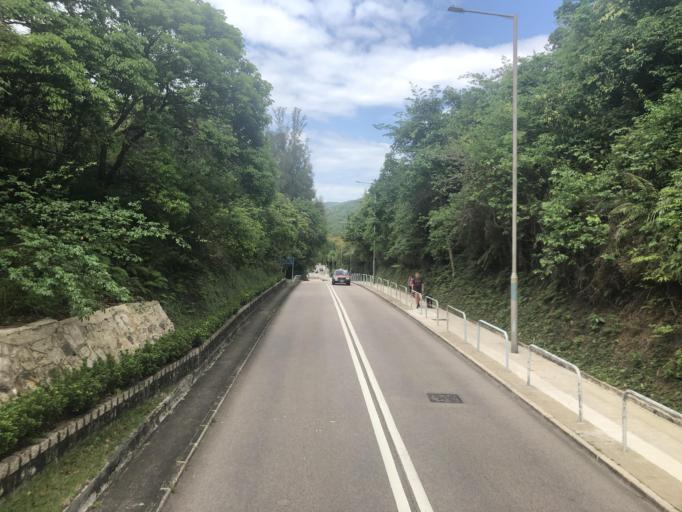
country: HK
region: Sai Kung
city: Sai Kung
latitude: 22.3955
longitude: 114.3178
